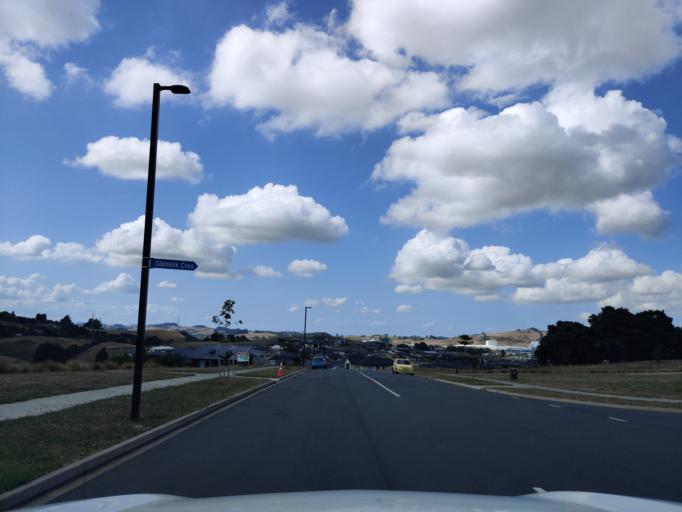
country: NZ
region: Auckland
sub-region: Auckland
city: Pukekohe East
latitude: -37.2339
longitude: 175.0144
